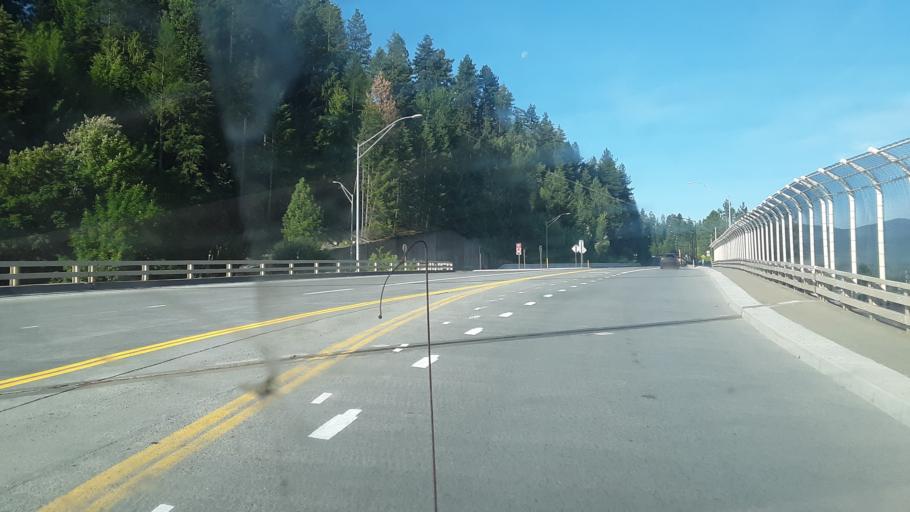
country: US
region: Idaho
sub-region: Boundary County
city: Bonners Ferry
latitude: 48.6959
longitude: -116.3099
